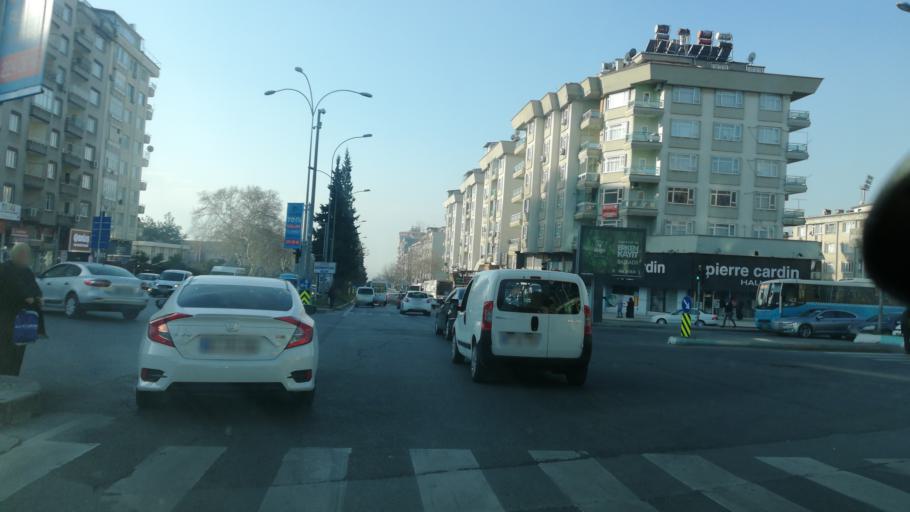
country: TR
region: Kahramanmaras
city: Kahramanmaras
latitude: 37.5750
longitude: 36.9262
